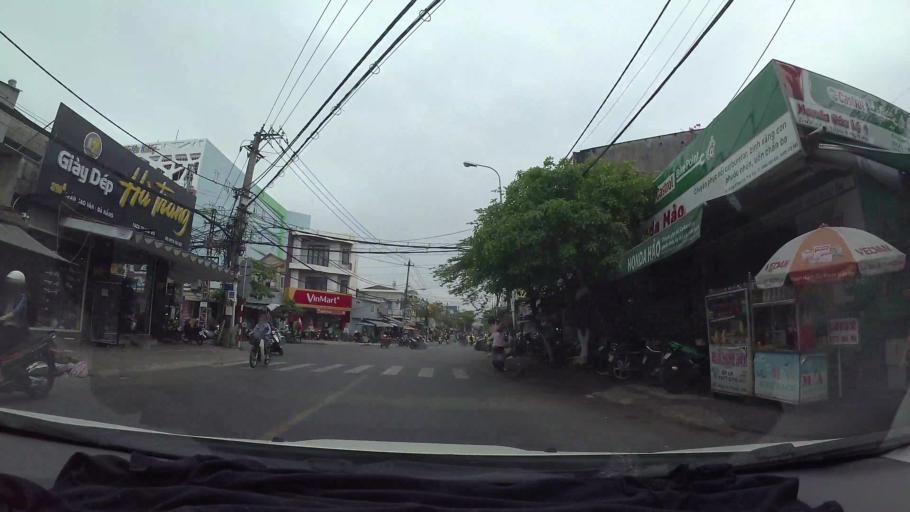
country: VN
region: Da Nang
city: Thanh Khe
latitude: 16.0677
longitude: 108.1820
